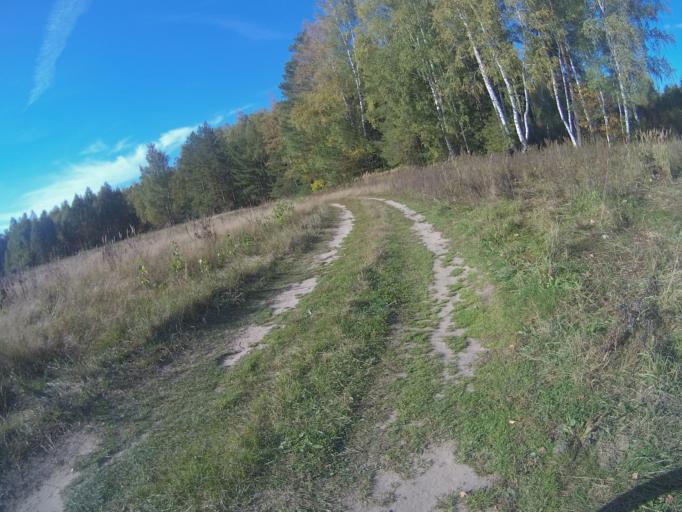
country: RU
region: Vladimir
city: Golovino
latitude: 55.9898
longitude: 40.4463
